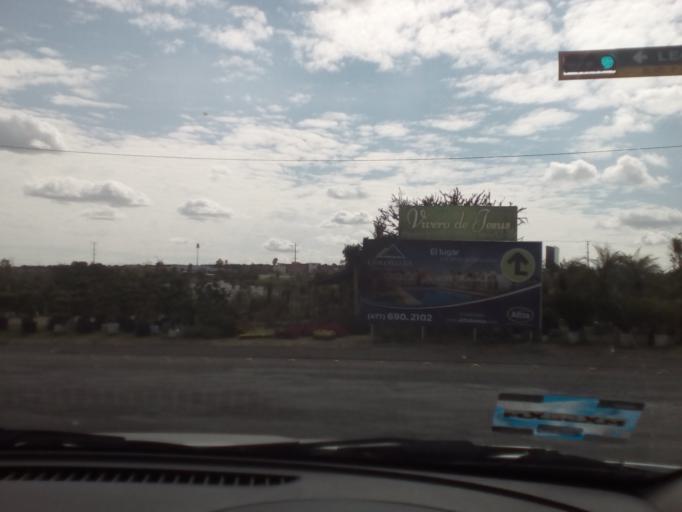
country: MX
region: Guanajuato
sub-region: Leon
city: La Ermita
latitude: 21.1731
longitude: -101.7357
